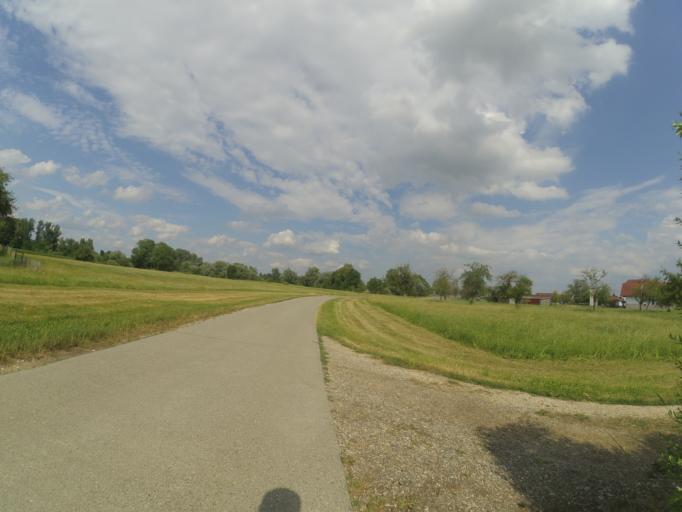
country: DE
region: Baden-Wuerttemberg
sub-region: Tuebingen Region
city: Ersingen
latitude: 48.2912
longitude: 9.8436
